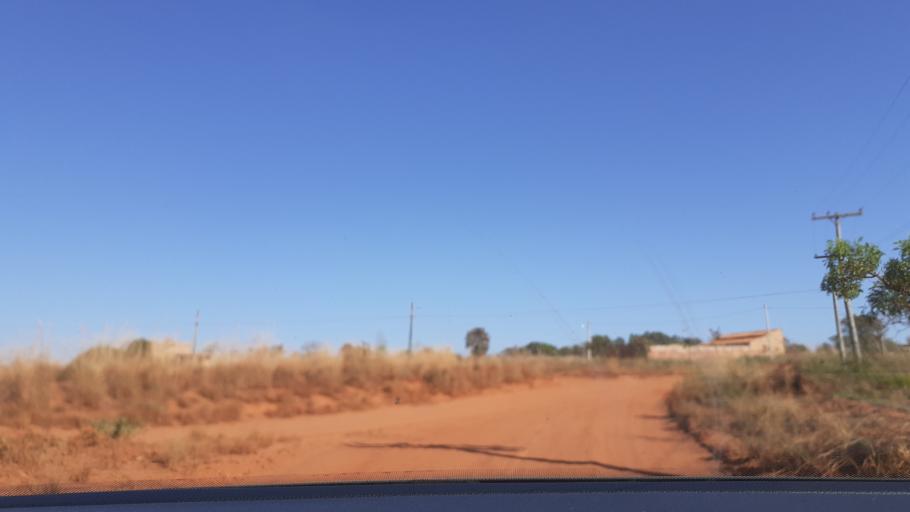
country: BR
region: Goias
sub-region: Aparecida De Goiania
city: Aparecida de Goiania
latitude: -16.8723
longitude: -49.2716
